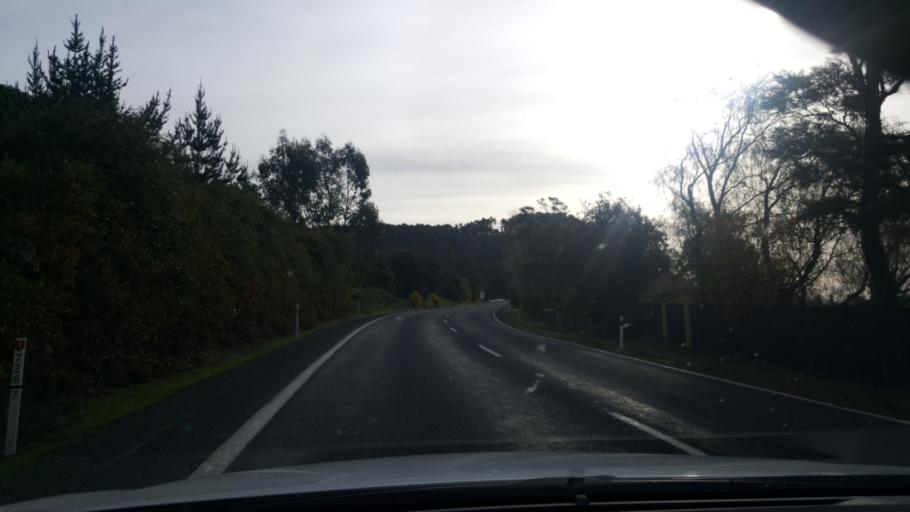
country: NZ
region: Waikato
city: Turangi
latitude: -38.8859
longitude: 175.9640
